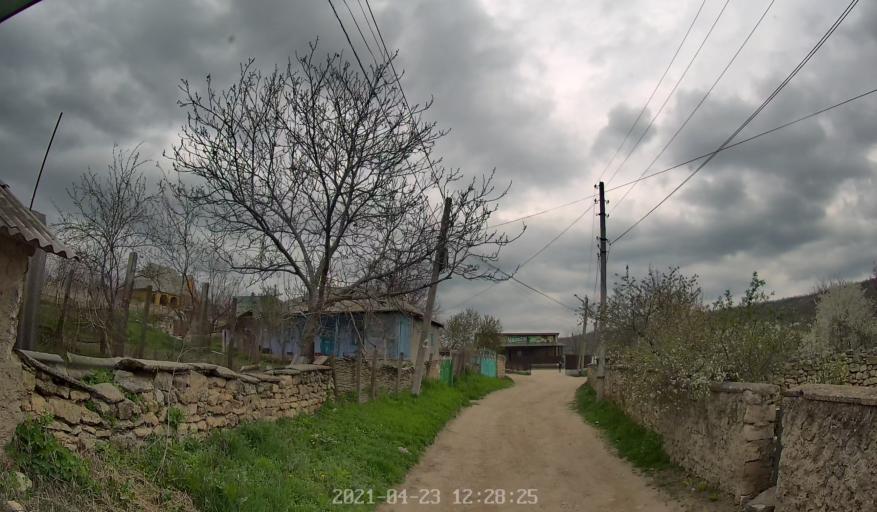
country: MD
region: Chisinau
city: Vadul lui Voda
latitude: 47.1273
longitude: 28.9998
